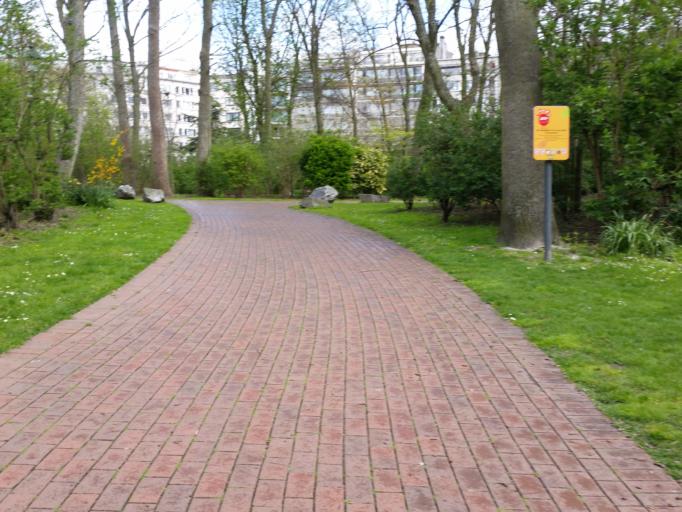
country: BE
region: Flanders
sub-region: Provincie West-Vlaanderen
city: Ostend
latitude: 51.2278
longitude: 2.9158
